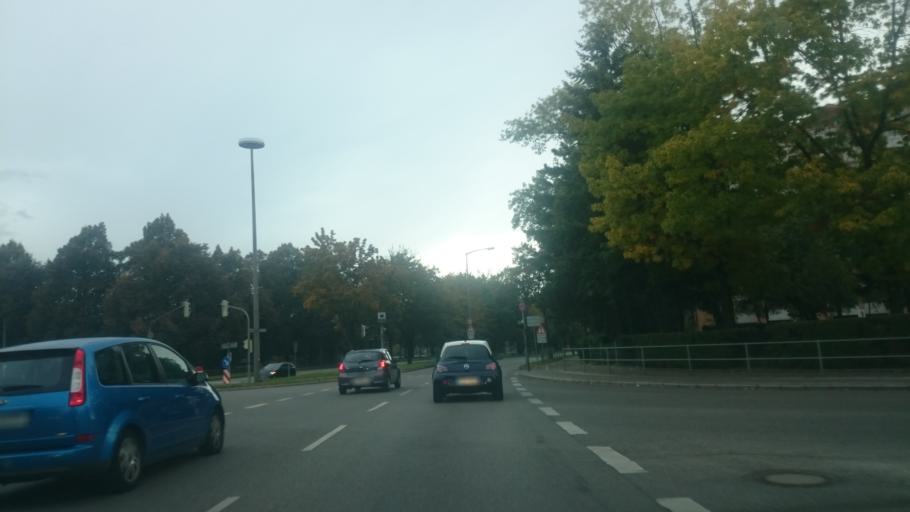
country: DE
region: Bavaria
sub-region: Swabia
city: Augsburg
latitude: 48.3855
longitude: 10.9075
